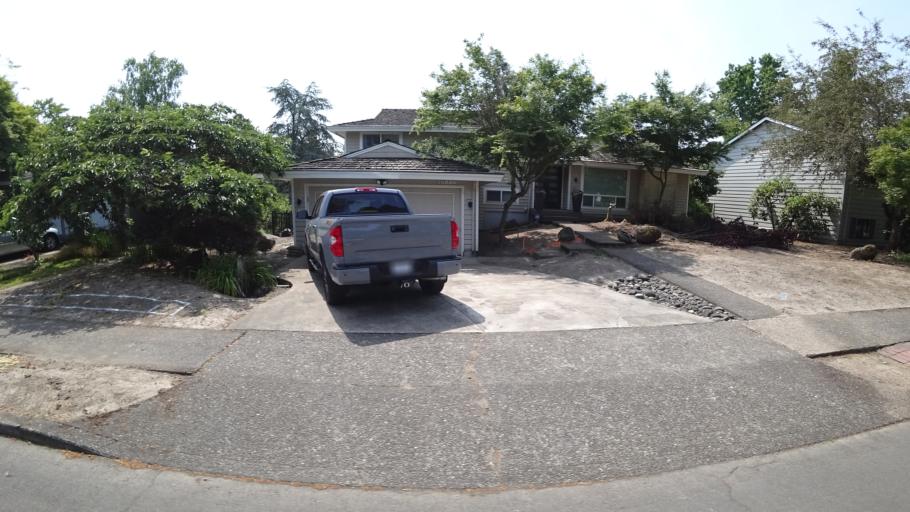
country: US
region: Oregon
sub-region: Washington County
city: Oak Hills
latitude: 45.5379
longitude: -122.8310
